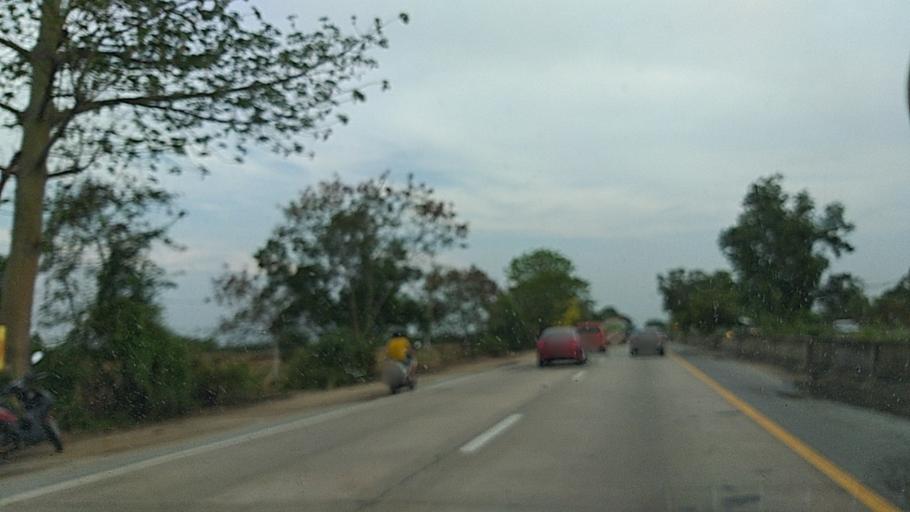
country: TH
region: Phra Nakhon Si Ayutthaya
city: Bang Pa-in
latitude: 14.1785
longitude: 100.5590
